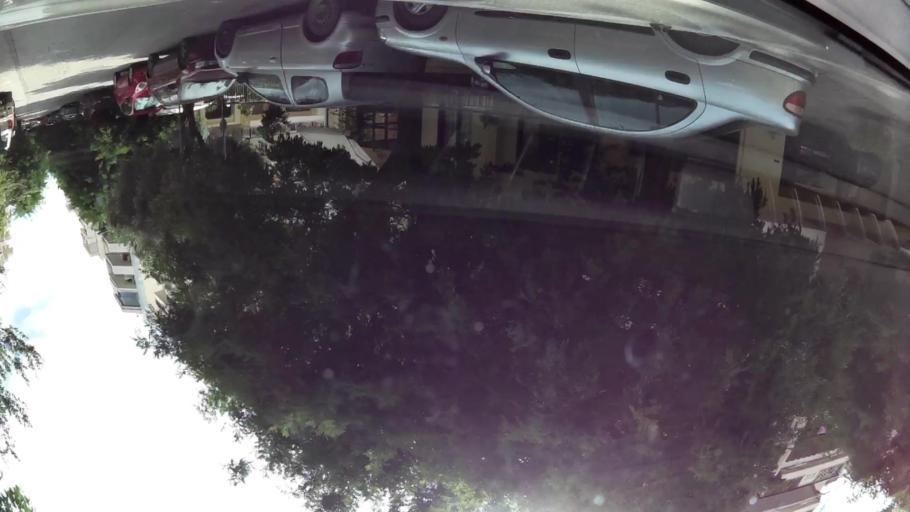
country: GR
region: Central Macedonia
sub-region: Nomos Thessalonikis
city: Triandria
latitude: 40.6051
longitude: 22.9779
